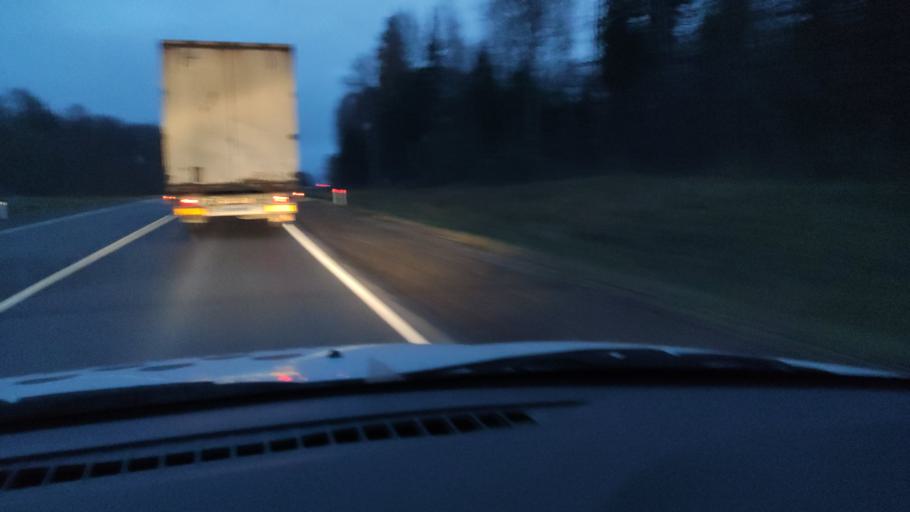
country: RU
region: Kirov
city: Kostino
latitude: 58.8338
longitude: 53.4974
